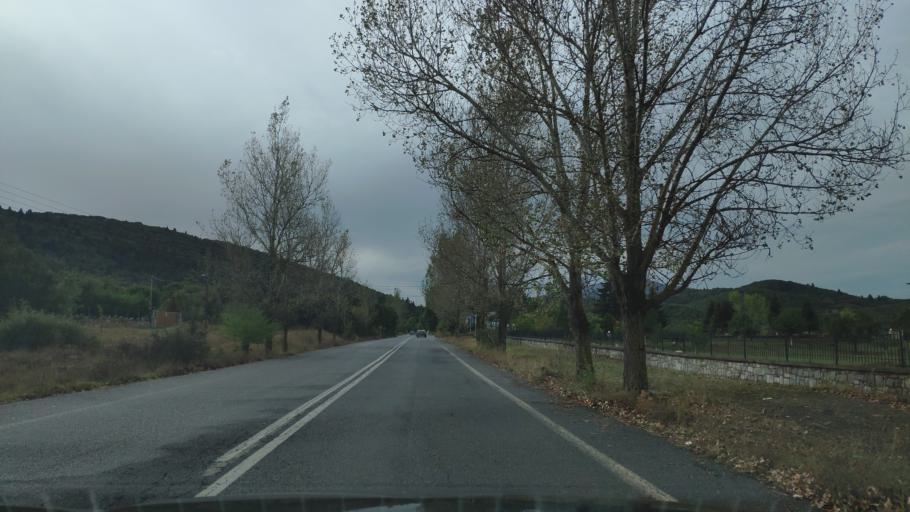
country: GR
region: Peloponnese
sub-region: Nomos Arkadias
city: Langadhia
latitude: 37.6912
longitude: 22.1959
